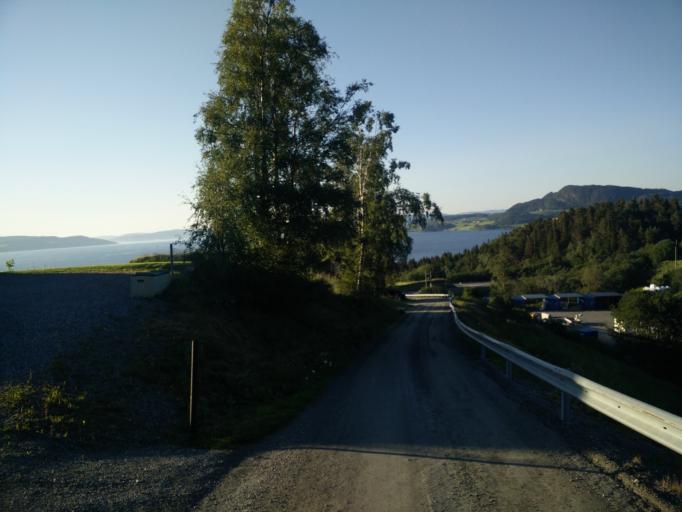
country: NO
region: Sor-Trondelag
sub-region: Skaun
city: Borsa
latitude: 63.3436
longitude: 10.0398
